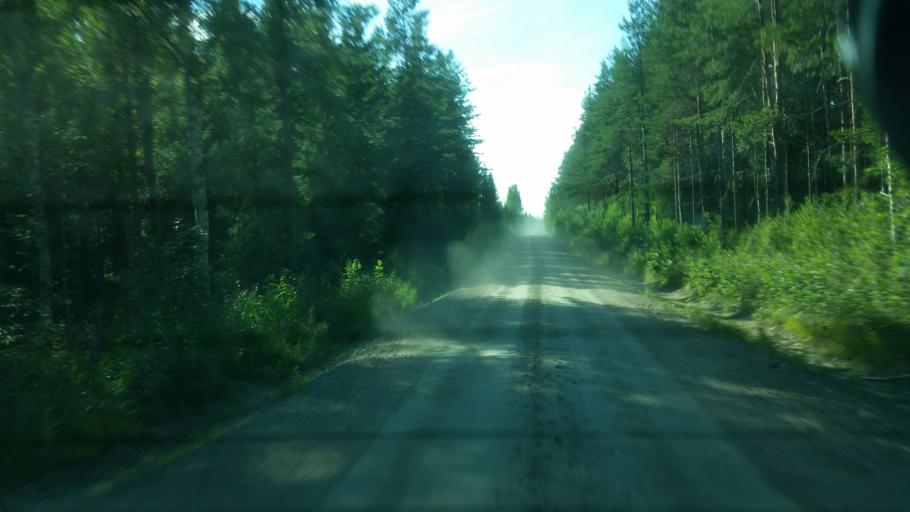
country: SE
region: Vaesternorrland
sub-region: Ange Kommun
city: Ange
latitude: 62.1950
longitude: 15.5916
